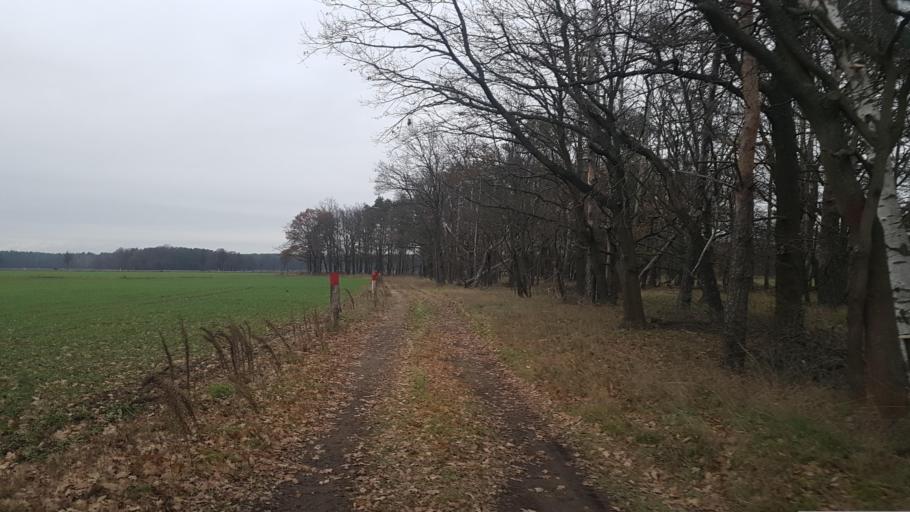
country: DE
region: Brandenburg
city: Cottbus
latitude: 51.7103
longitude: 14.4208
